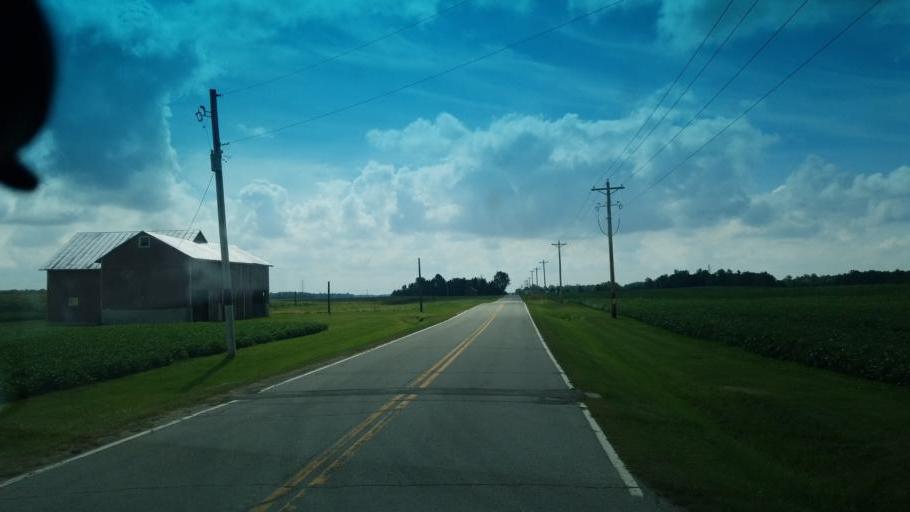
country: US
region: Ohio
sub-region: Crawford County
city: Bucyrus
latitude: 40.9559
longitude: -82.9017
